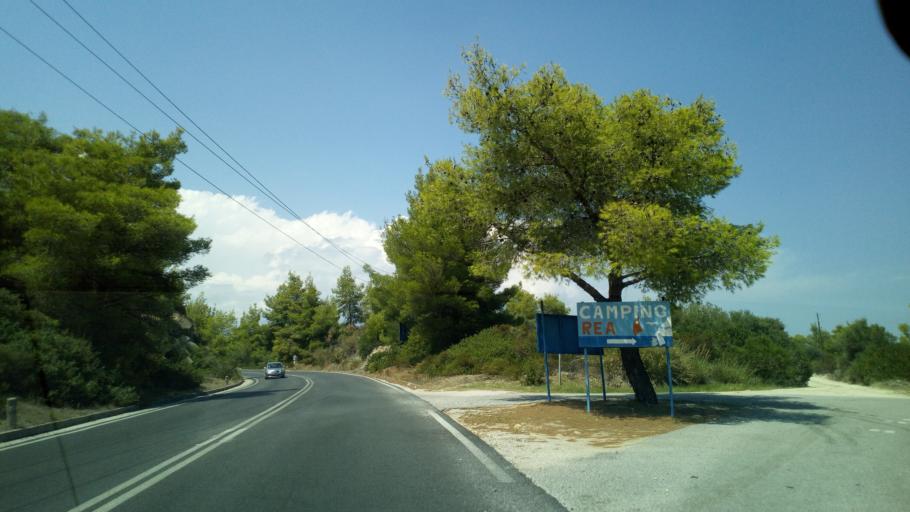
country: GR
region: Central Macedonia
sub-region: Nomos Chalkidikis
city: Agios Nikolaos
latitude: 40.2080
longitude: 23.7599
